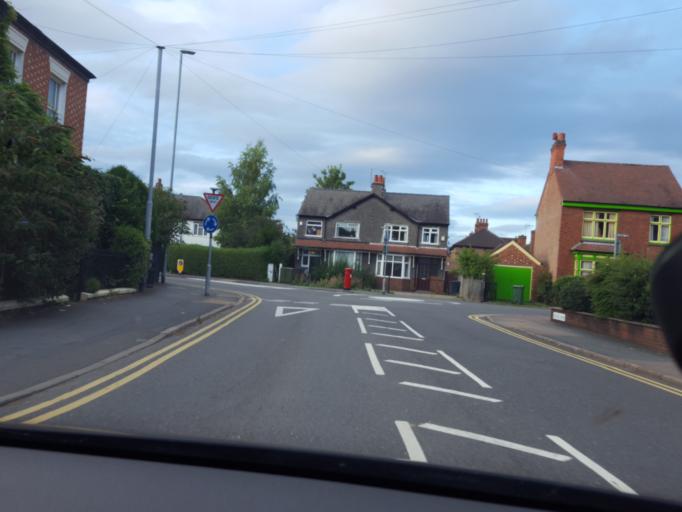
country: GB
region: England
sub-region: Leicestershire
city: Loughborough
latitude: 52.7659
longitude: -1.2091
